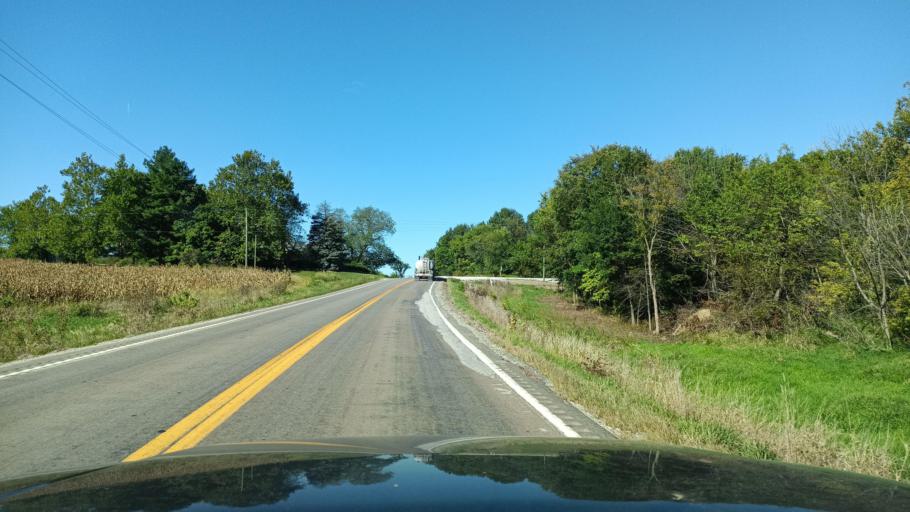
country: US
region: Missouri
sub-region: Scotland County
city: Memphis
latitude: 40.4553
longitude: -92.0567
